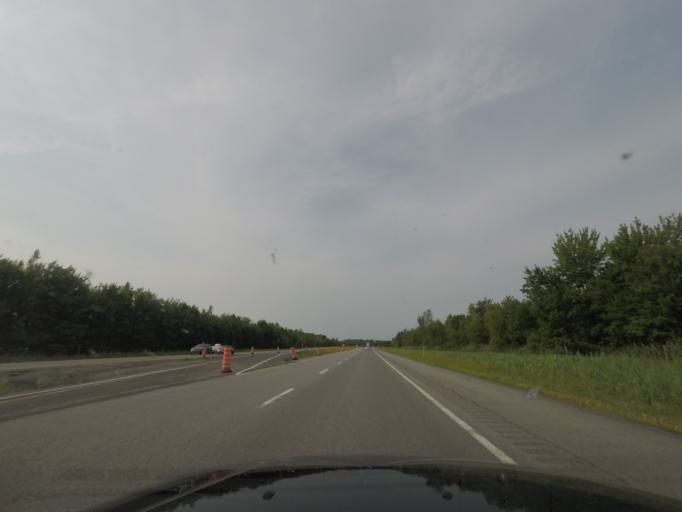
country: CA
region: Quebec
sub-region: Monteregie
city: Napierville
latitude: 45.1575
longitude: -73.4676
